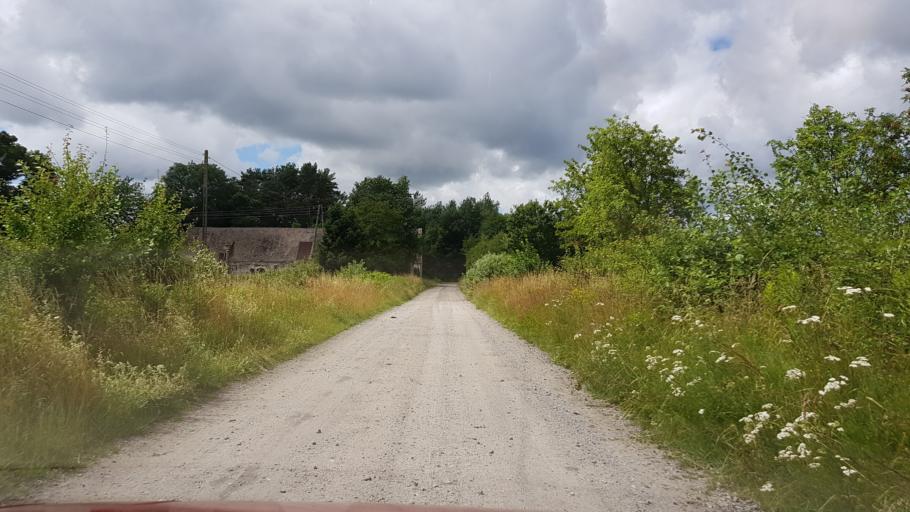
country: PL
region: West Pomeranian Voivodeship
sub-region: Powiat bialogardzki
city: Karlino
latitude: 54.1639
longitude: 15.9331
